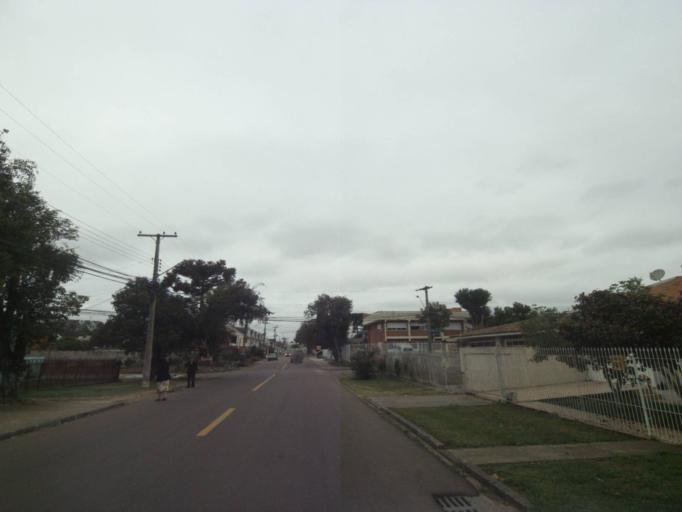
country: BR
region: Parana
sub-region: Pinhais
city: Pinhais
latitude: -25.4774
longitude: -49.2401
